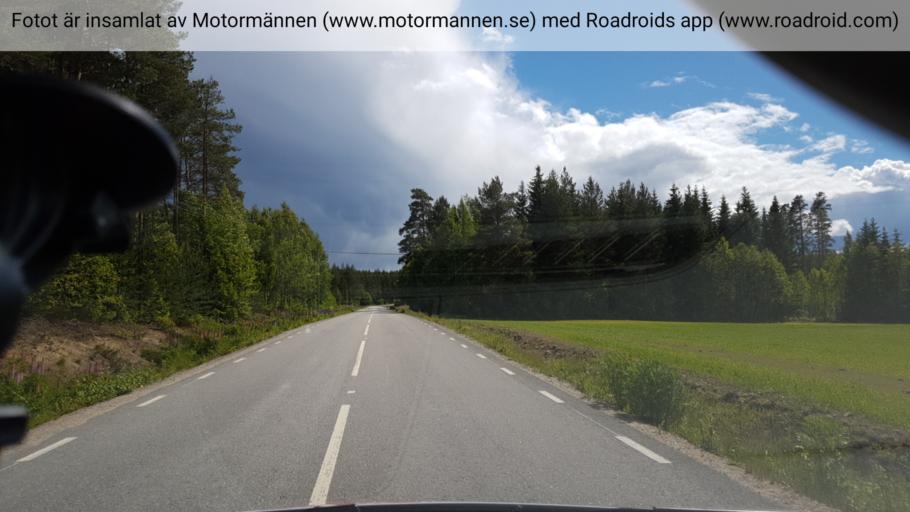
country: SE
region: Gaevleborg
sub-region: Bollnas Kommun
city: Vittsjo
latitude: 61.2351
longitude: 16.1495
